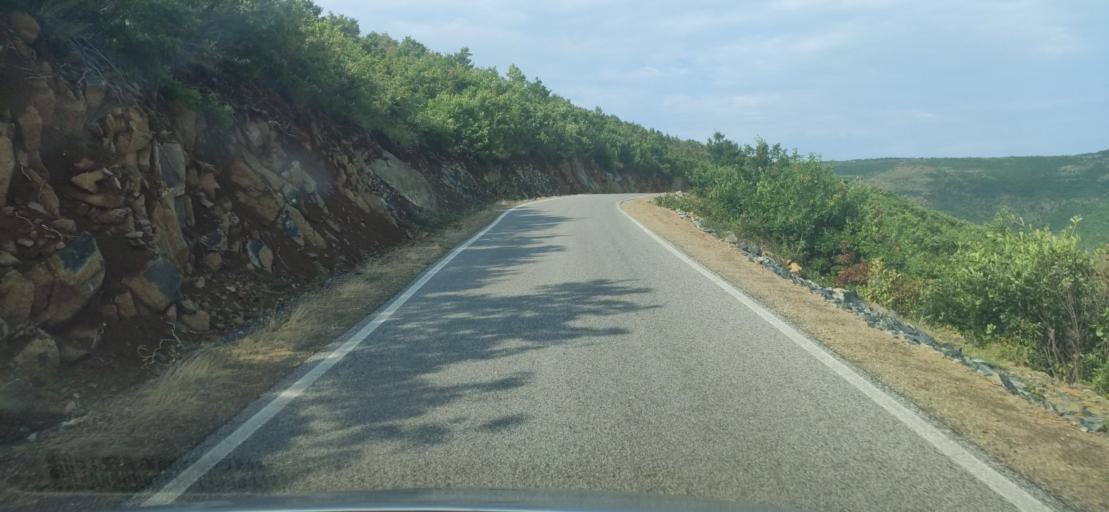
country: AL
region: Shkoder
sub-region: Rrethi i Pukes
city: Iballe
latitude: 42.1737
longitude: 19.9949
